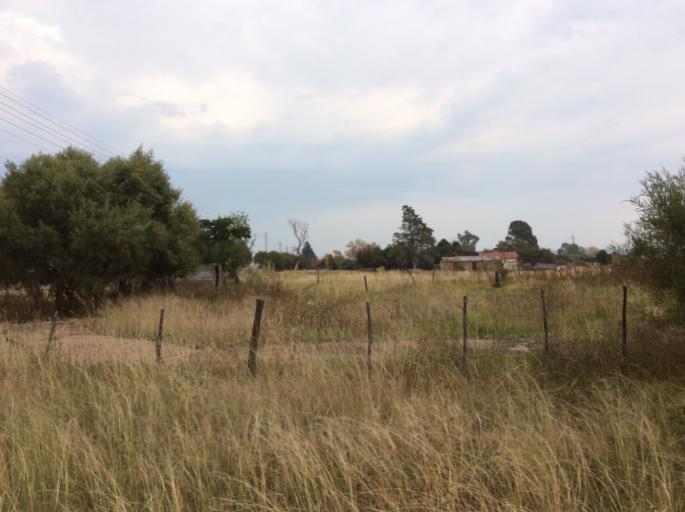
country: LS
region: Mafeteng
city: Mafeteng
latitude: -29.9886
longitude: 27.0163
